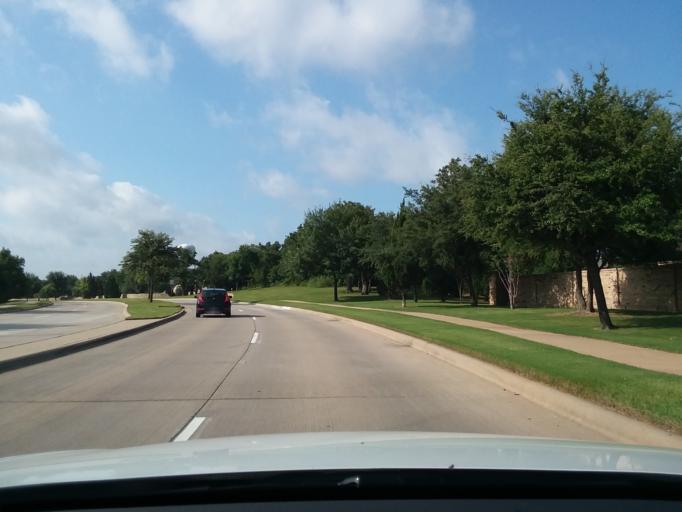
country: US
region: Texas
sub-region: Denton County
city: Bartonville
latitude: 33.0796
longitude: -97.1264
